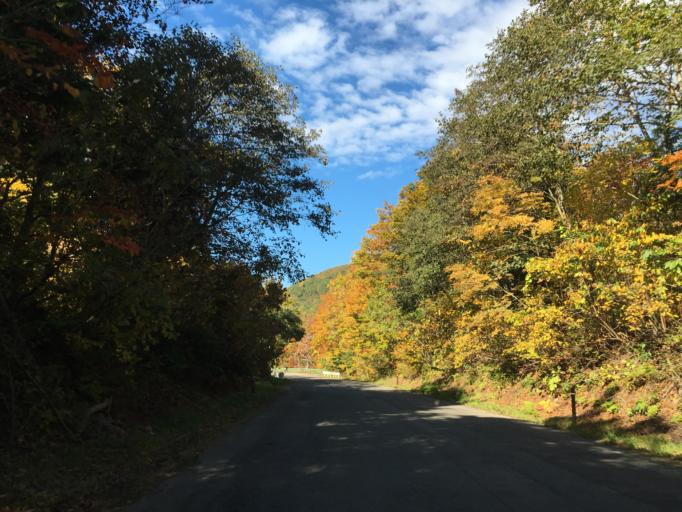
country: JP
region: Fukushima
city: Inawashiro
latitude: 37.6049
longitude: 140.2430
